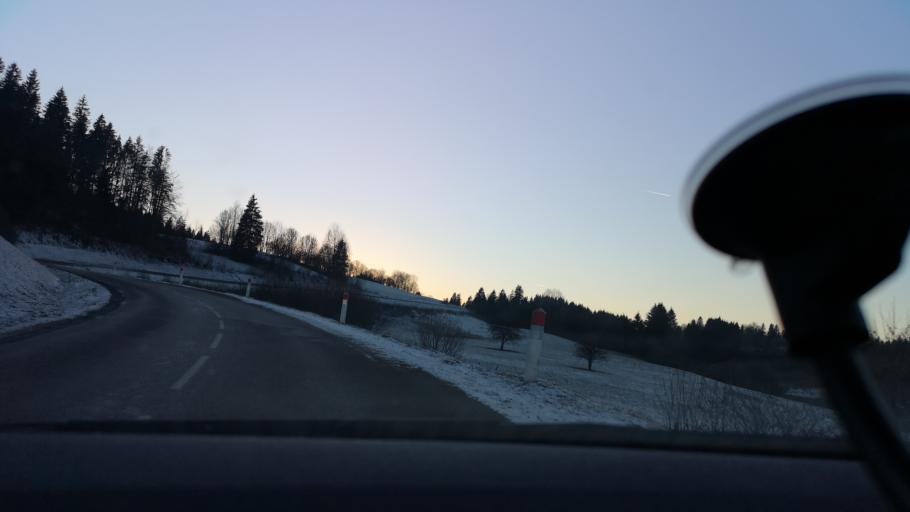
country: FR
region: Franche-Comte
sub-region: Departement du Doubs
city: Pontarlier
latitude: 46.8509
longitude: 6.3261
